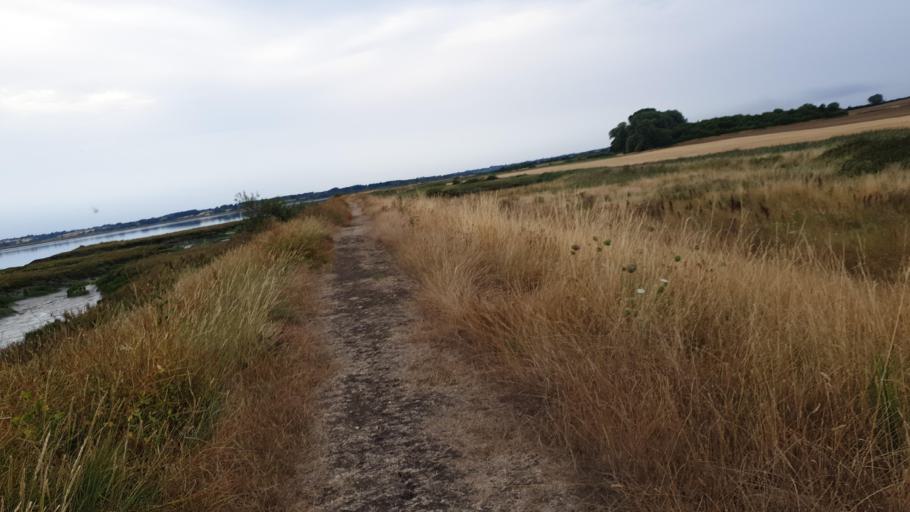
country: GB
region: England
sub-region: Essex
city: Brightlingsea
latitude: 51.8181
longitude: 0.9939
